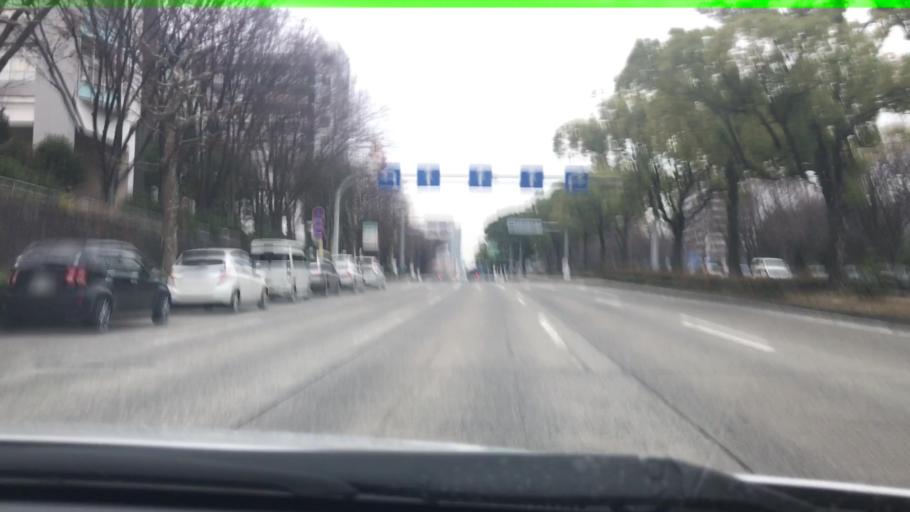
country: JP
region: Aichi
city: Nagoya-shi
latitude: 35.1850
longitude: 136.9049
